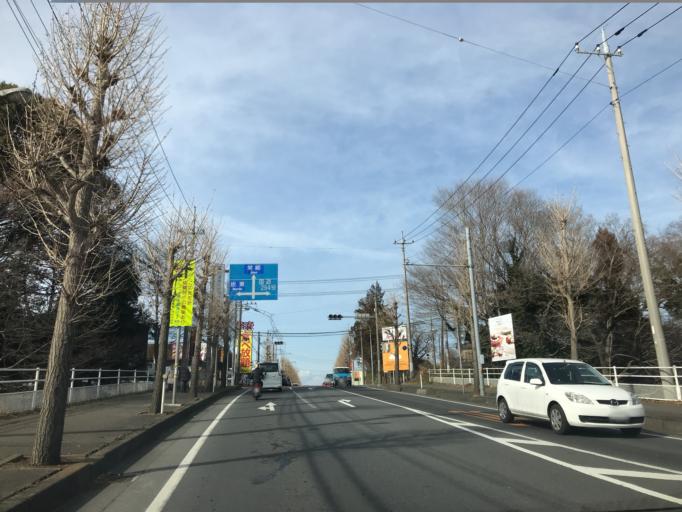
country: JP
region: Ibaraki
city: Moriya
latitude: 35.9264
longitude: 139.9974
